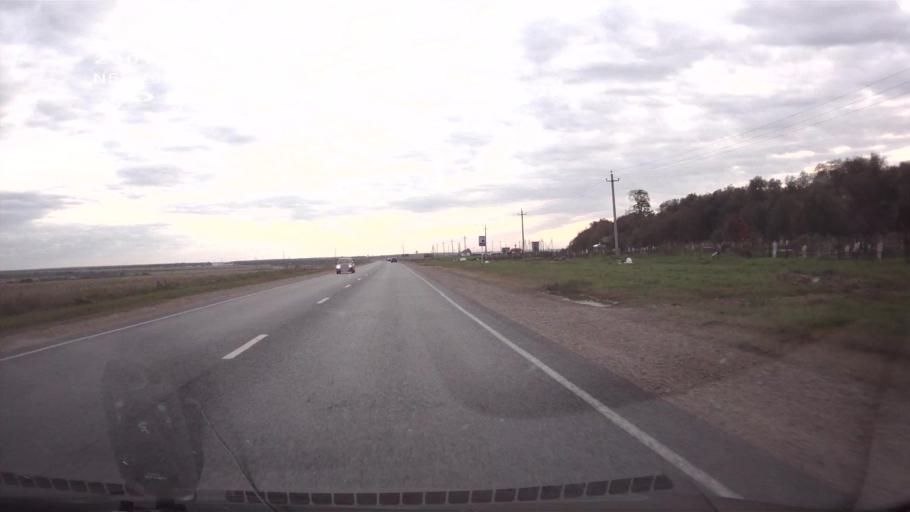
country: RU
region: Mariy-El
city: Yoshkar-Ola
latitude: 56.6990
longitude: 48.0646
